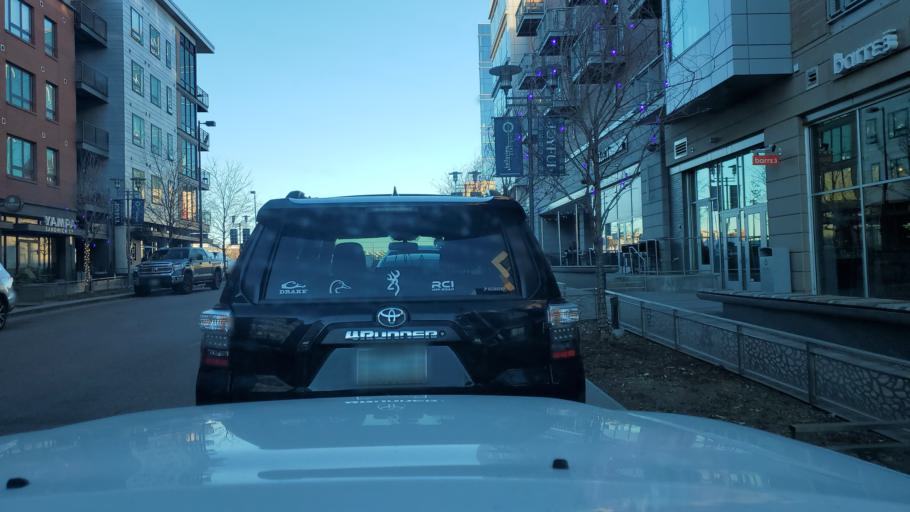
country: US
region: Colorado
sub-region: Arapahoe County
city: Castlewood
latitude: 39.6247
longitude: -104.9069
